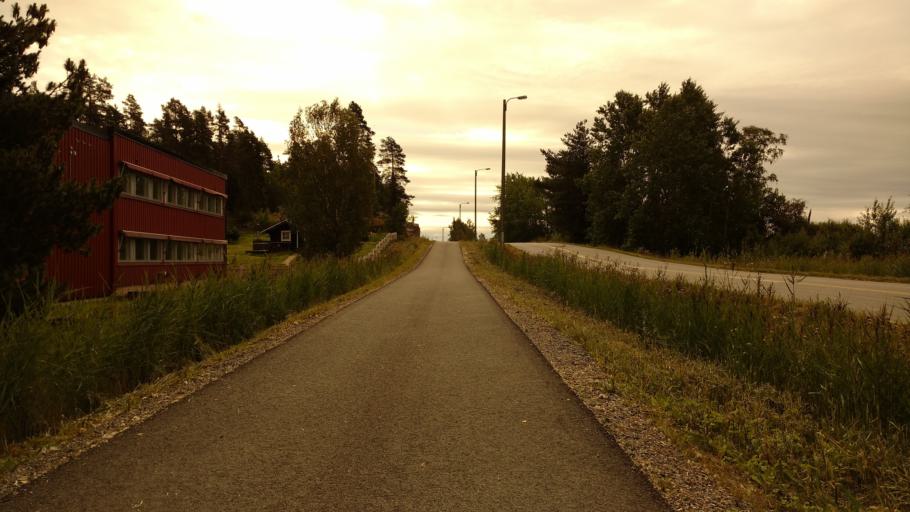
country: FI
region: Varsinais-Suomi
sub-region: Turku
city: Piikkioe
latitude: 60.4314
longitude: 22.4732
